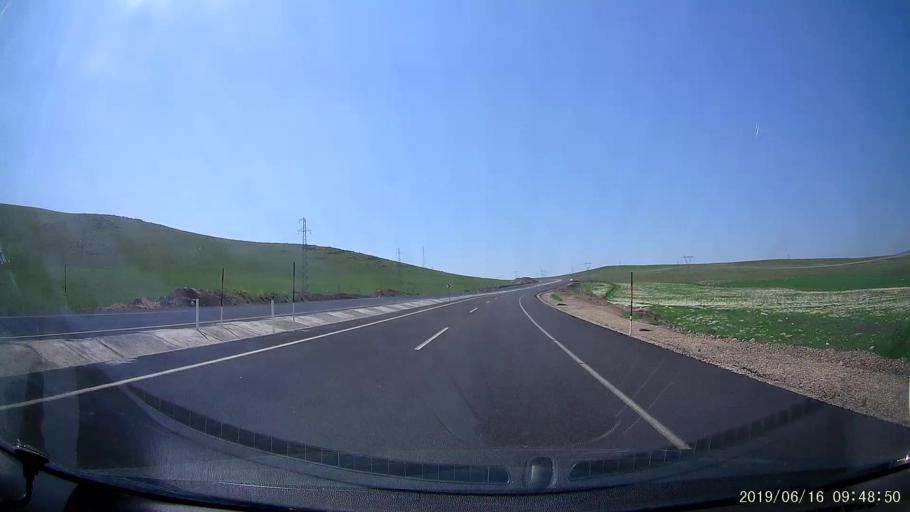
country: TR
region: Kars
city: Digor
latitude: 40.4287
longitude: 43.3560
